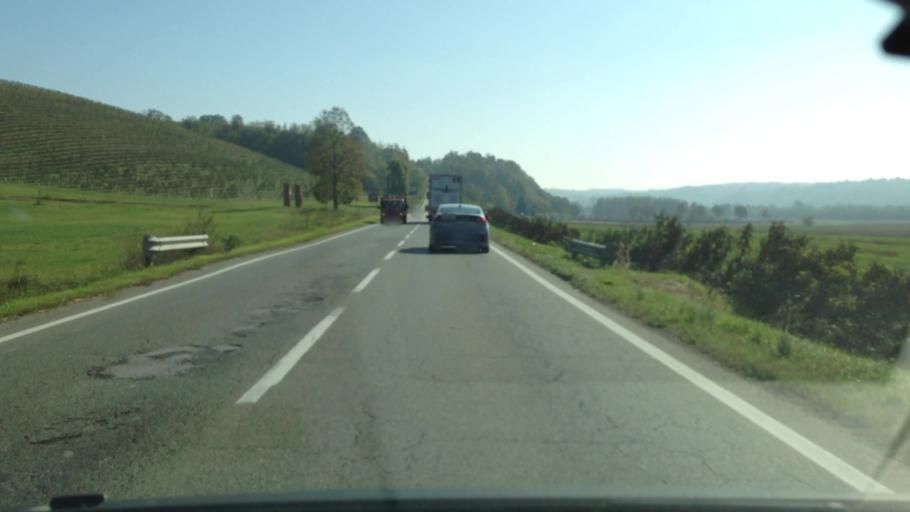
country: IT
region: Piedmont
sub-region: Provincia di Asti
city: Castello di Annone
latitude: 44.8956
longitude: 8.2976
